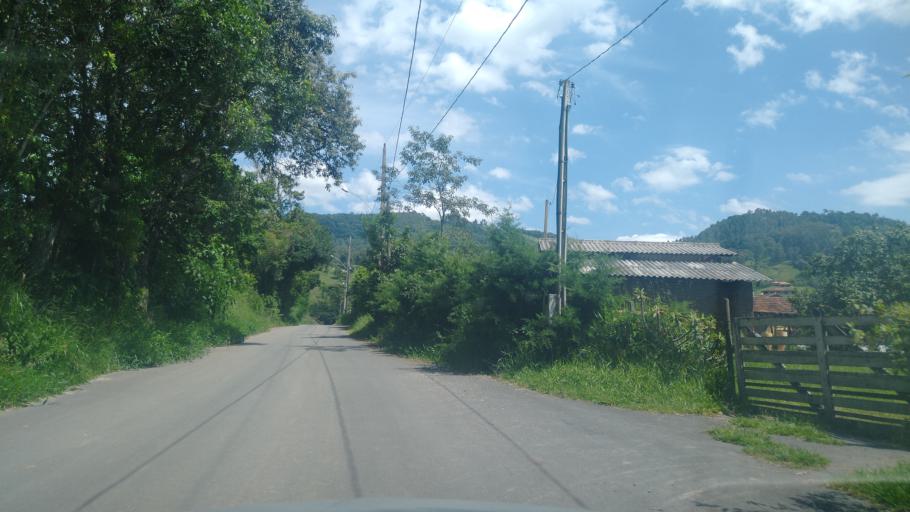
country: BR
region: Minas Gerais
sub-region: Extrema
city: Extrema
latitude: -22.7634
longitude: -46.2838
